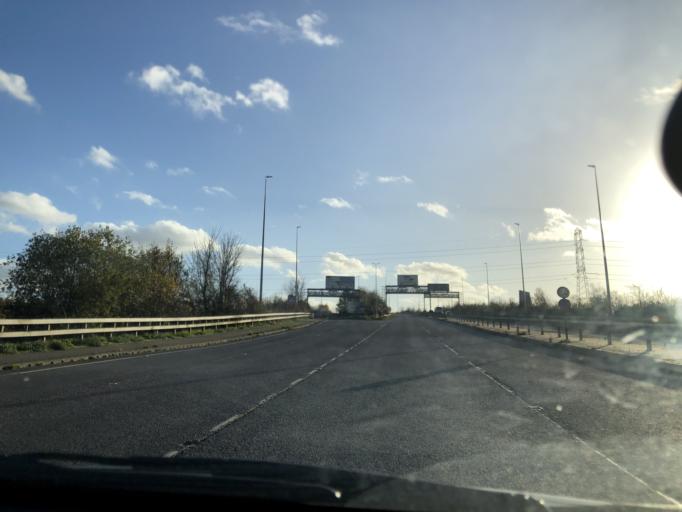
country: GB
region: England
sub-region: Kent
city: Greenhithe
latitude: 51.4368
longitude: 0.2786
